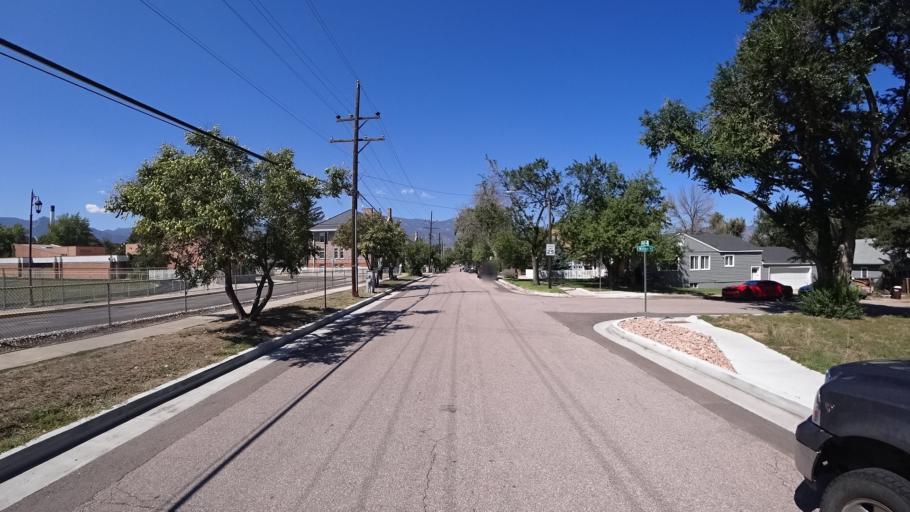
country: US
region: Colorado
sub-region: El Paso County
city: Colorado Springs
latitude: 38.8359
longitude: -104.8044
